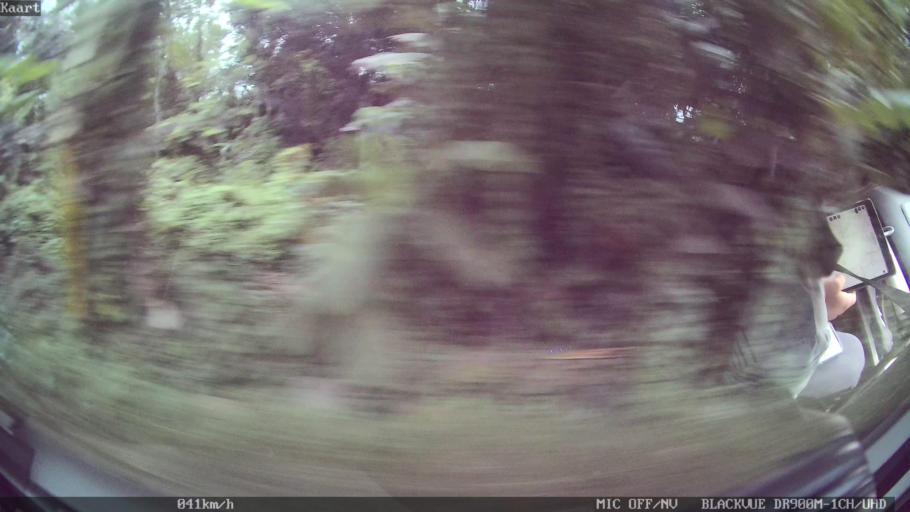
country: ID
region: Bali
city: Banjar Parekan
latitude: -8.5714
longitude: 115.2098
